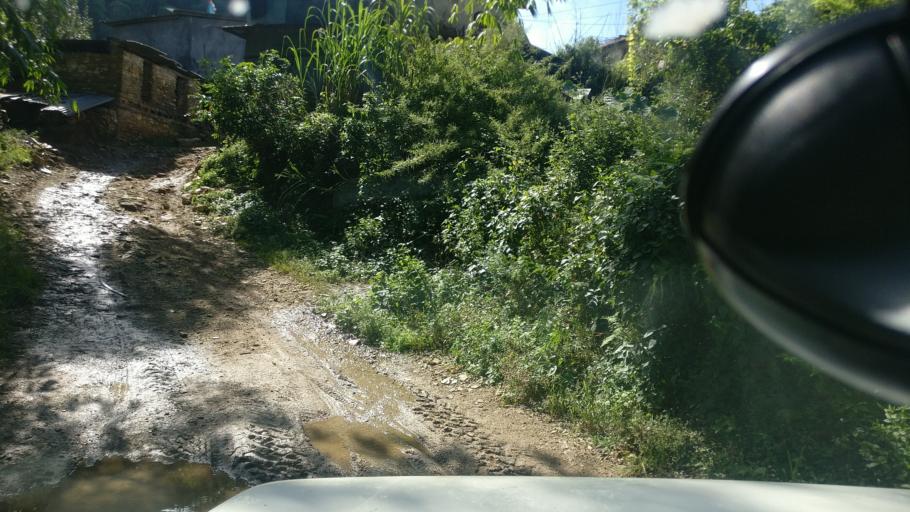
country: NP
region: Western Region
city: Waling
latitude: 28.1188
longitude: 83.6754
